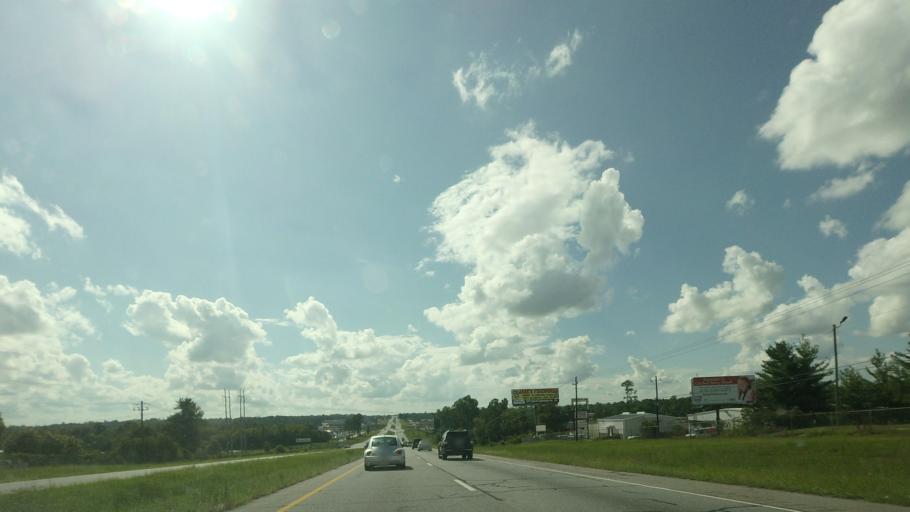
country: US
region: Georgia
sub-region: Bibb County
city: Macon
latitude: 32.8149
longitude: -83.6768
